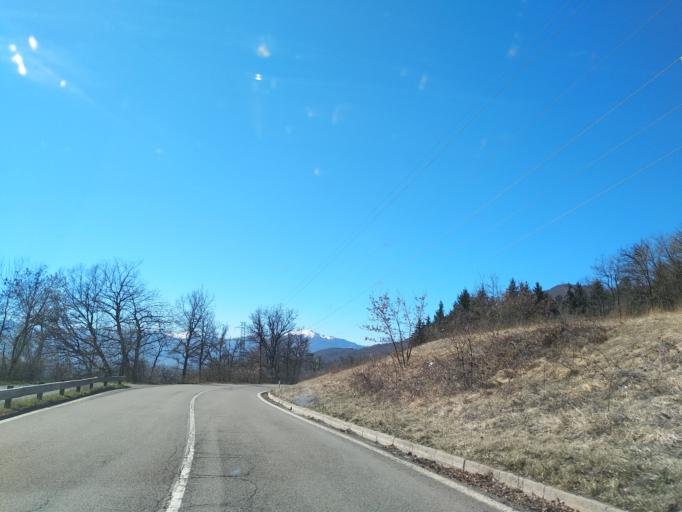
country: IT
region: Emilia-Romagna
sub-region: Provincia di Reggio Emilia
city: Busana
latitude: 44.4075
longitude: 10.3377
